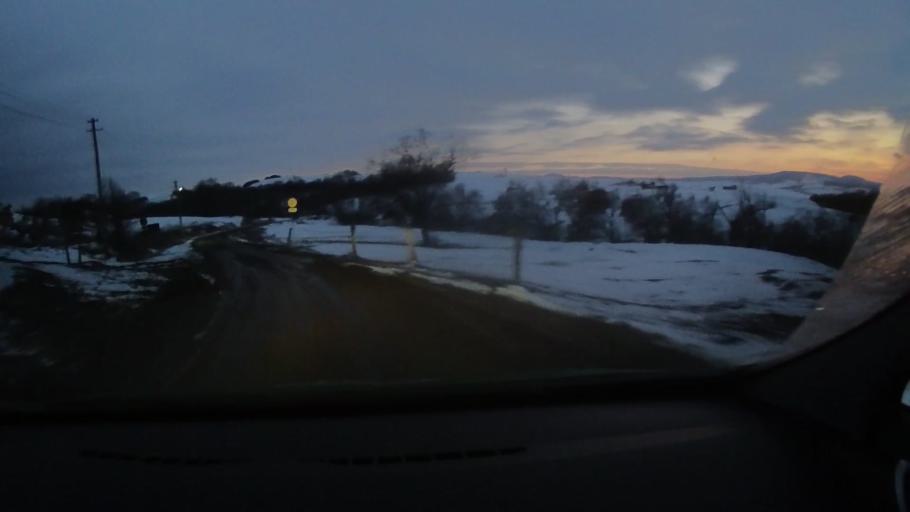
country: RO
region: Harghita
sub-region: Comuna Darjiu
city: Darjiu
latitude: 46.1691
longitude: 25.2272
